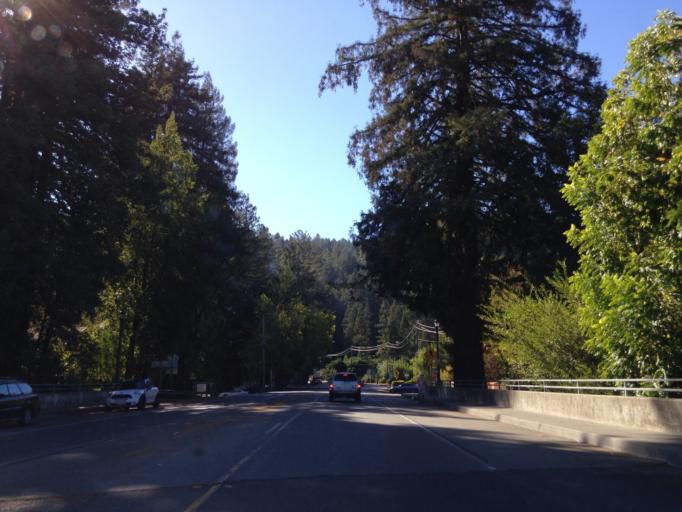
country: US
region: California
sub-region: Sonoma County
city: Guerneville
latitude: 38.5020
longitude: -123.0012
